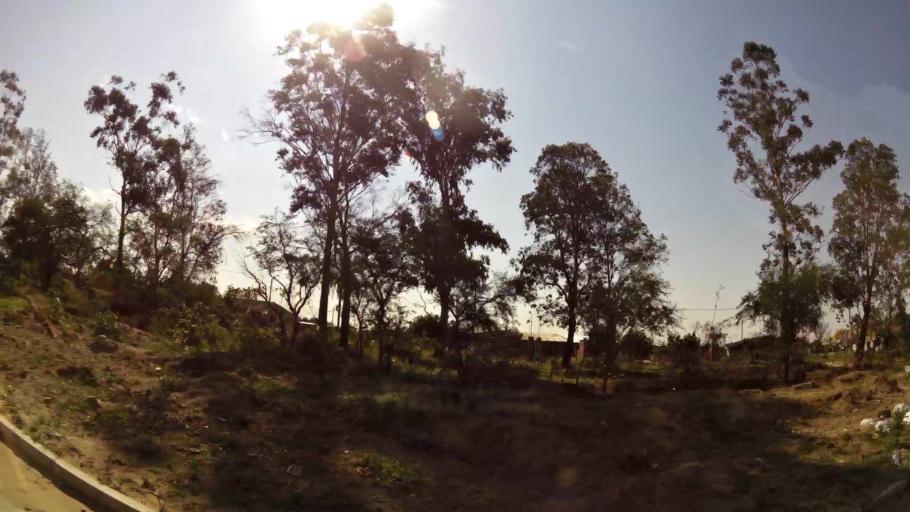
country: BO
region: Santa Cruz
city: Cotoca
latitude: -17.7497
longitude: -63.0886
